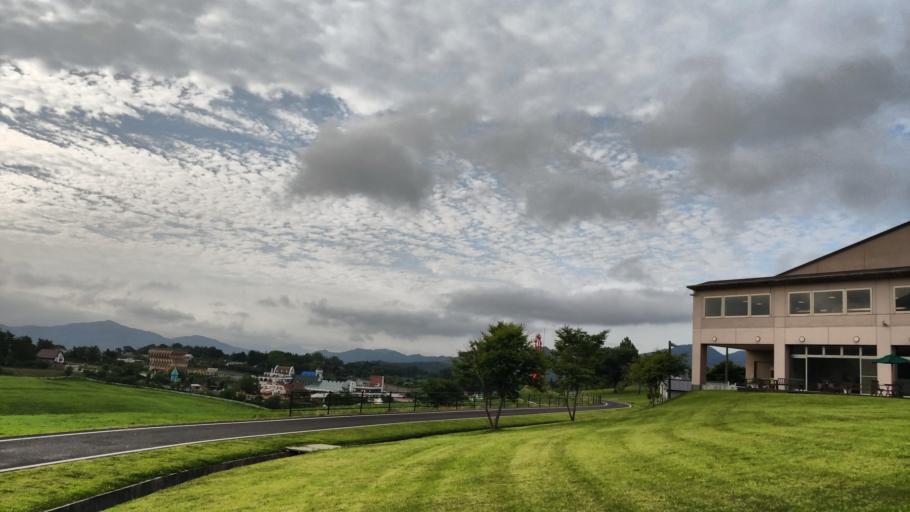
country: JP
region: Tottori
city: Kurayoshi
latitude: 35.2946
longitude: 133.6315
